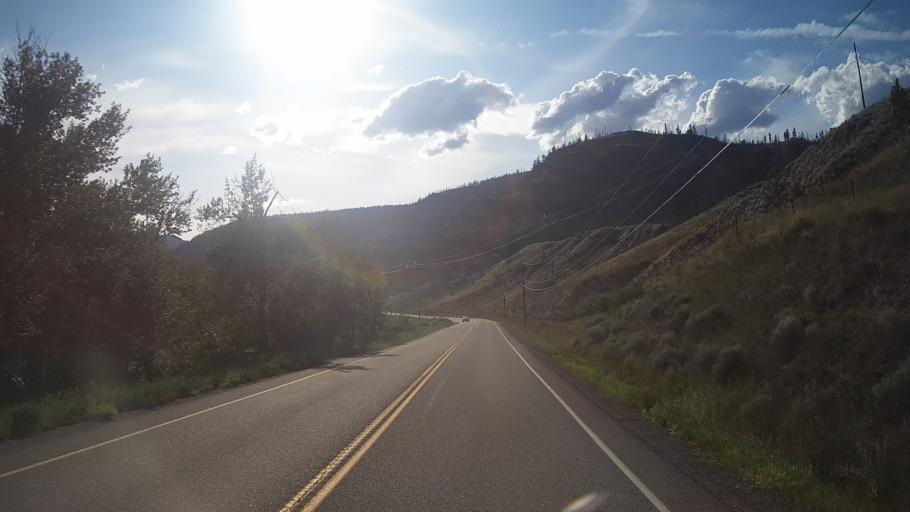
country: CA
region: British Columbia
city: Cache Creek
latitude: 50.8843
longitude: -121.4772
